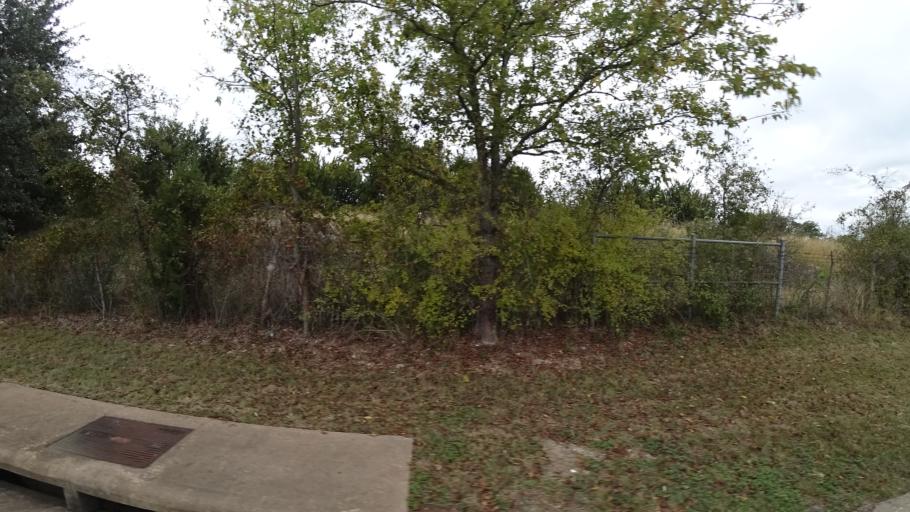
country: US
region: Texas
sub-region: Williamson County
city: Round Rock
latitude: 30.5102
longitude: -97.7011
